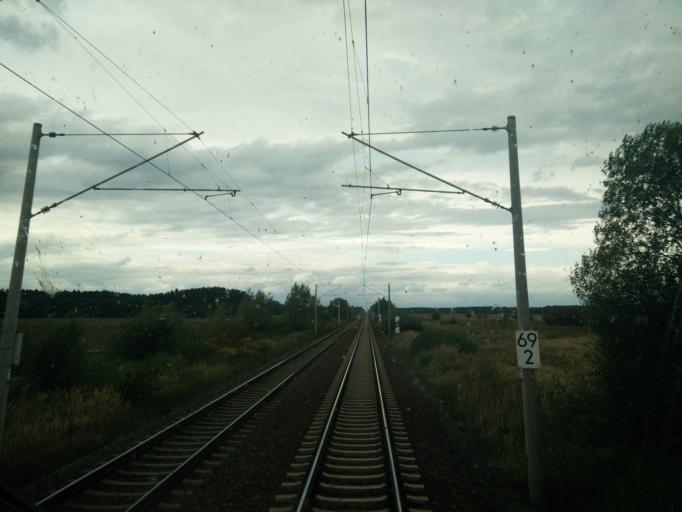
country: DE
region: Brandenburg
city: Luebben
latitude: 51.9674
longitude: 13.8138
